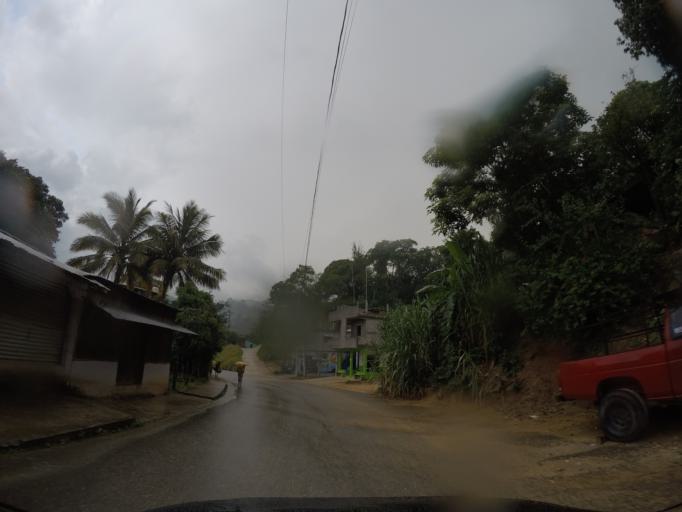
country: MX
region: Oaxaca
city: San Gabriel Mixtepec
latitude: 16.0901
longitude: -97.0805
